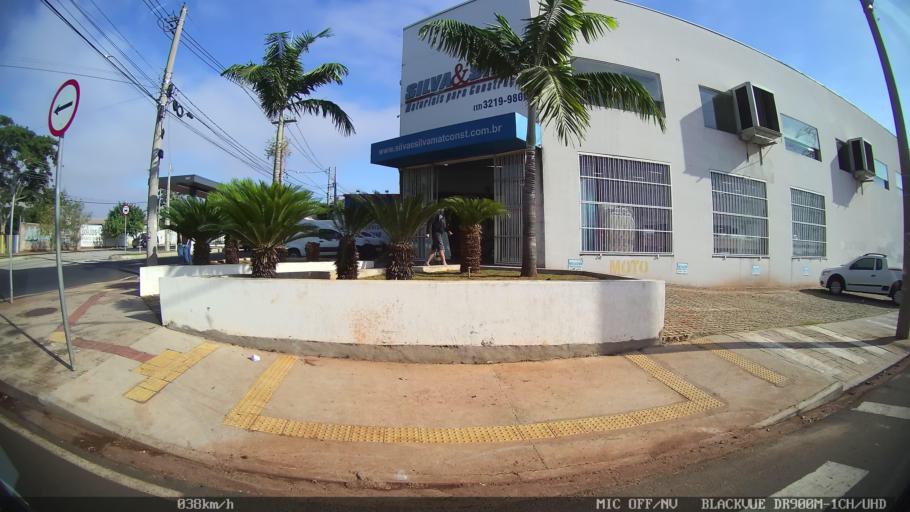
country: BR
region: Sao Paulo
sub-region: Sao Jose Do Rio Preto
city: Sao Jose do Rio Preto
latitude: -20.7934
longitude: -49.4155
